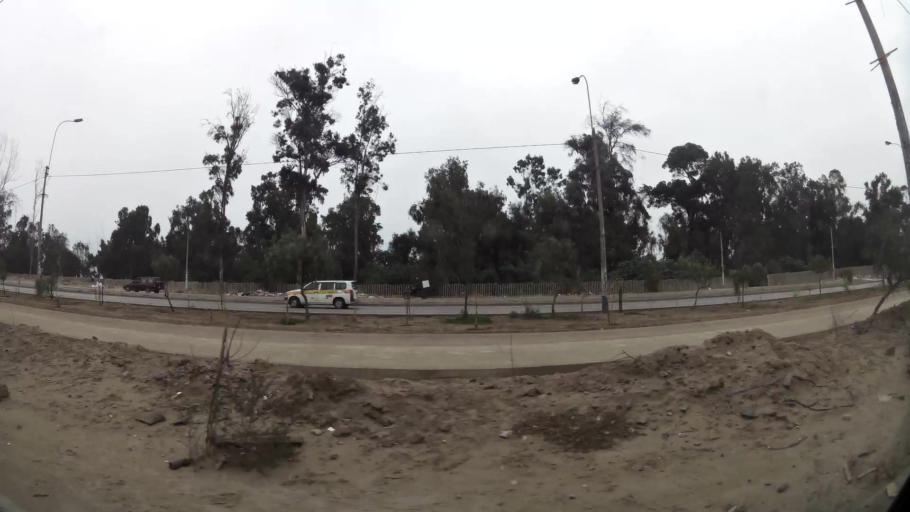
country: PE
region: Lima
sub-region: Lima
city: Surco
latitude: -12.1997
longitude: -76.9565
